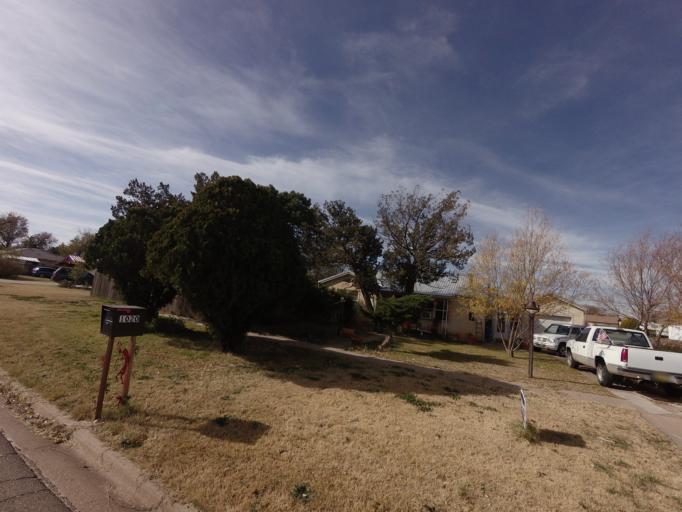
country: US
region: New Mexico
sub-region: Curry County
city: Clovis
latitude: 34.4087
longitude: -103.1927
